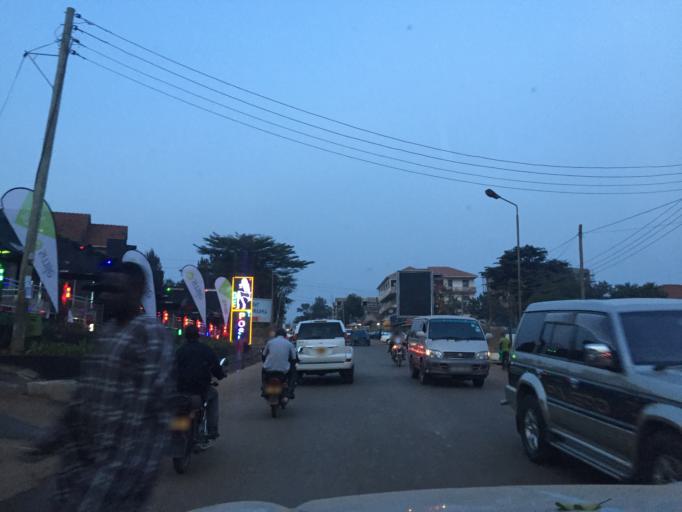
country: UG
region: Central Region
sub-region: Kampala District
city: Kampala
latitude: 0.2988
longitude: 32.6027
